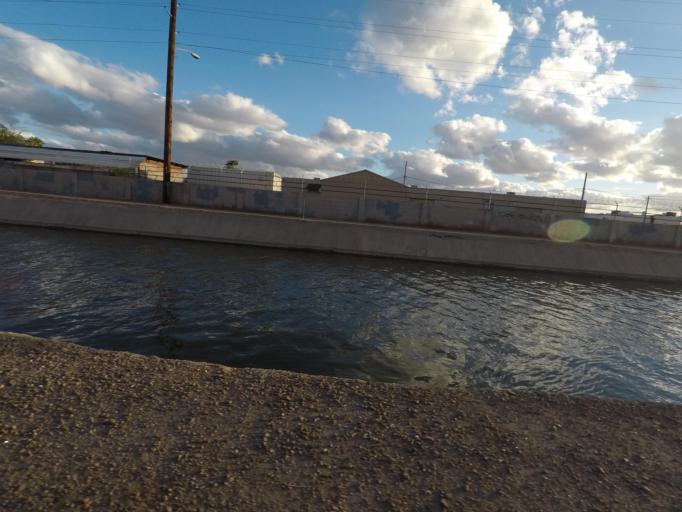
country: US
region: Arizona
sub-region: Maricopa County
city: Phoenix
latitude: 33.4887
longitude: -112.1305
